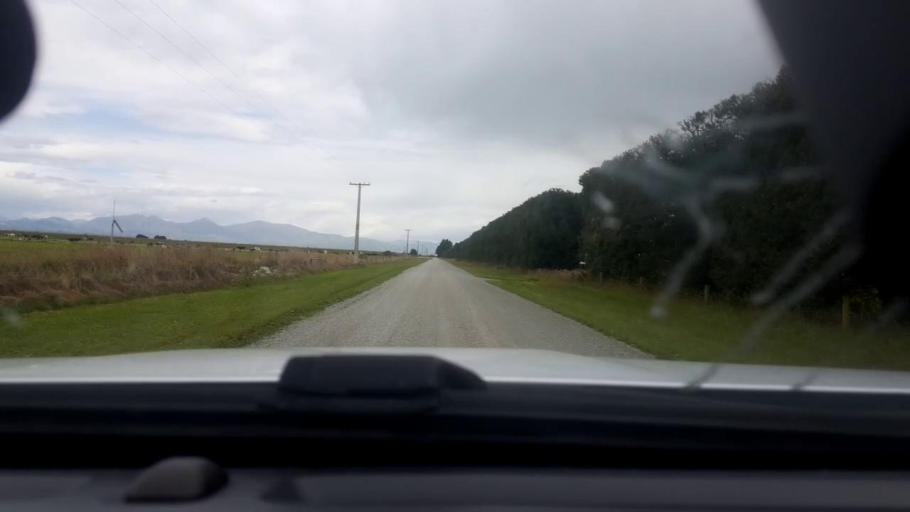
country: NZ
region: Canterbury
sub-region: Timaru District
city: Pleasant Point
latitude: -44.1484
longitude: 171.3919
